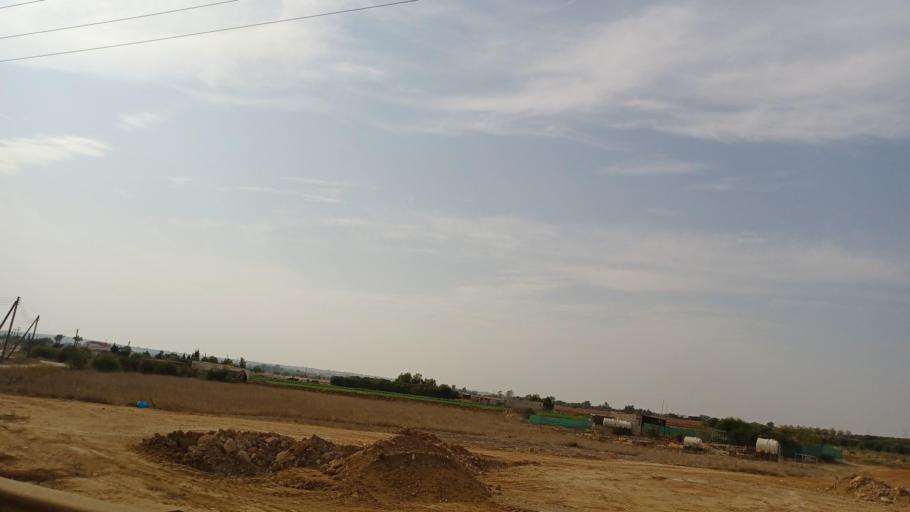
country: CY
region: Ammochostos
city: Liopetri
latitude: 34.9963
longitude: 33.8921
